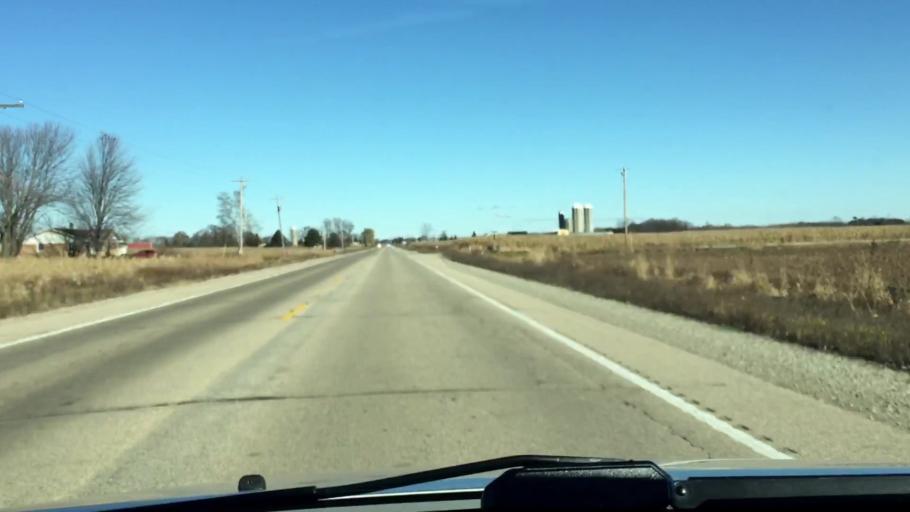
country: US
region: Wisconsin
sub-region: Brown County
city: Pulaski
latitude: 44.6210
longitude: -88.2204
